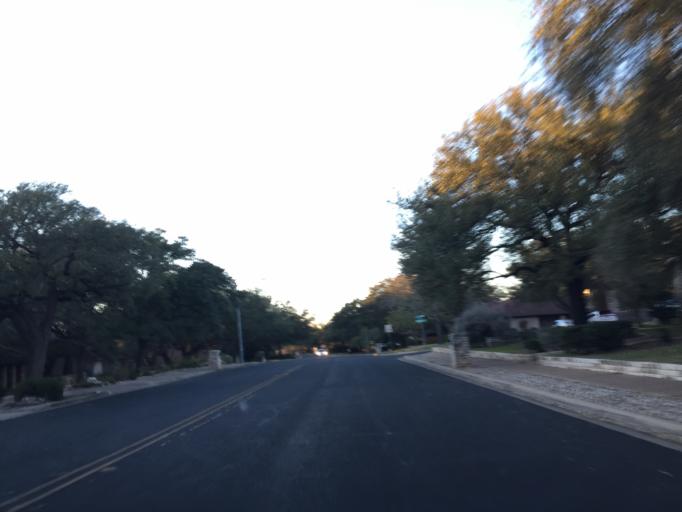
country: US
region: Texas
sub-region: Williamson County
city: Jollyville
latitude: 30.3953
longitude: -97.7550
